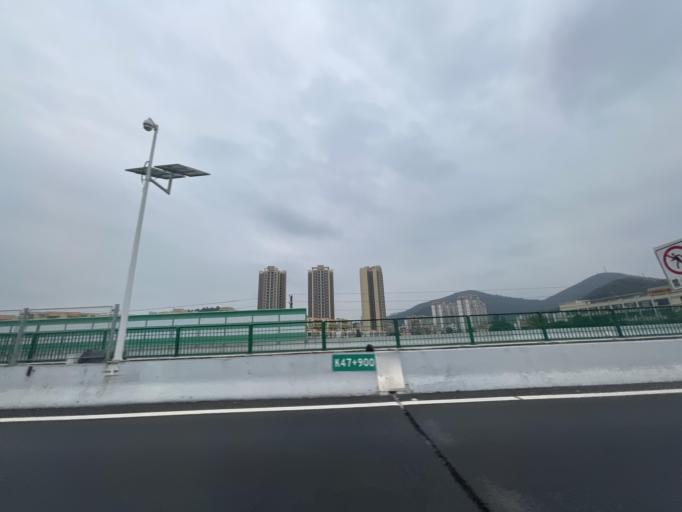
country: CN
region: Guangdong
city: Nansha
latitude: 22.7807
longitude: 113.5380
